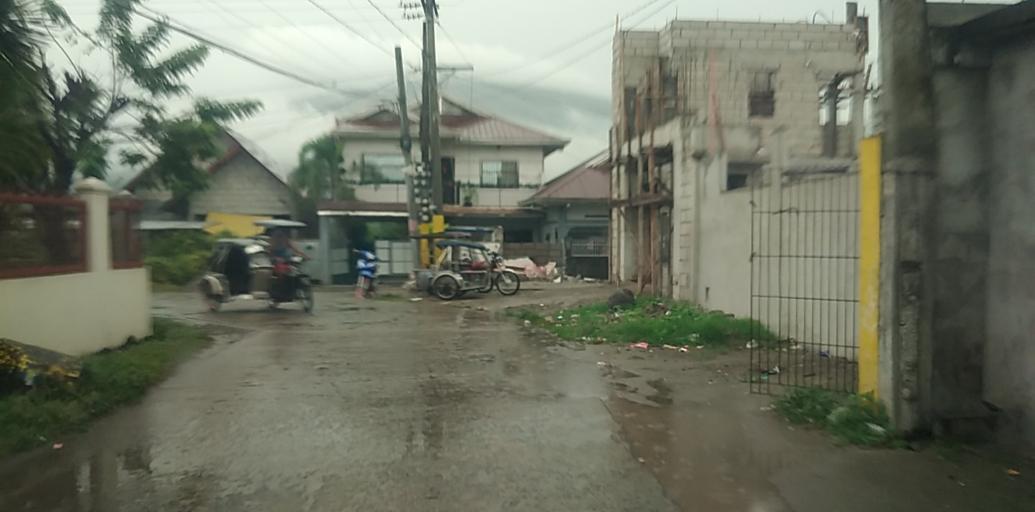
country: PH
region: Central Luzon
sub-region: Province of Pampanga
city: Panlinlang
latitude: 15.1567
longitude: 120.7235
